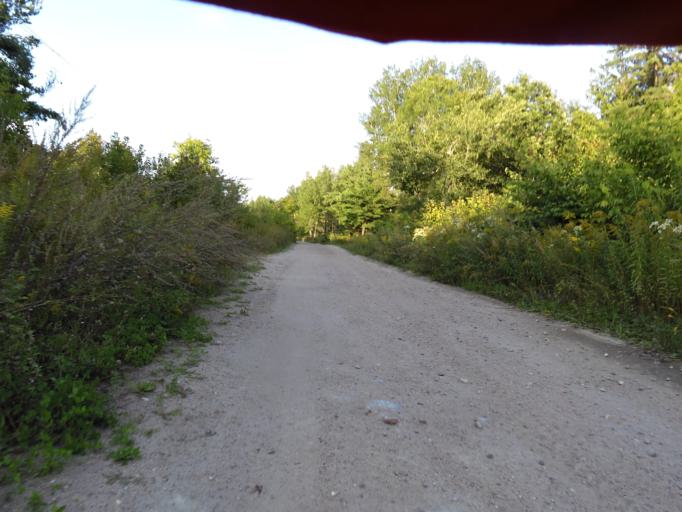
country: CA
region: Quebec
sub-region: Outaouais
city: Maniwaki
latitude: 46.3687
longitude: -75.9811
